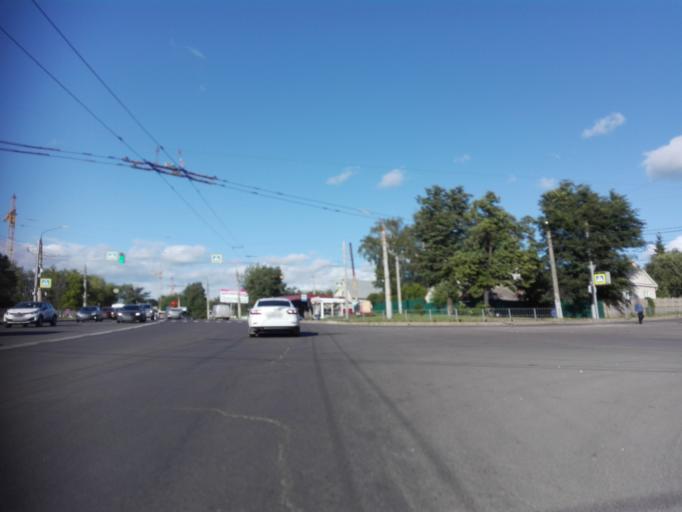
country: RU
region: Orjol
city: Orel
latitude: 52.9862
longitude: 36.1165
